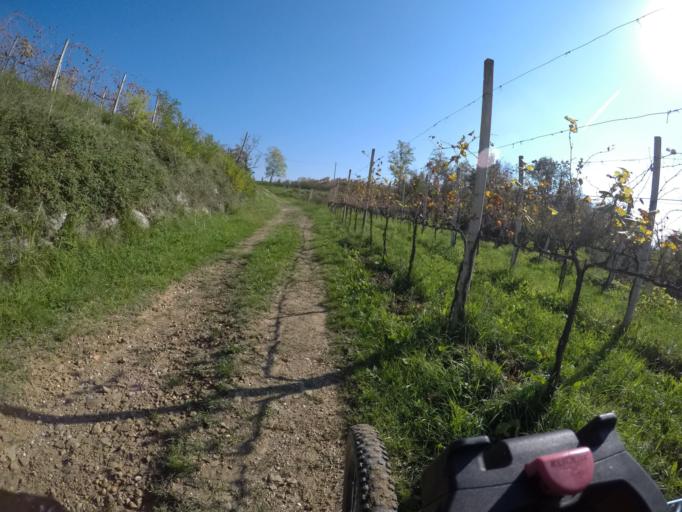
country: IT
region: Friuli Venezia Giulia
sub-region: Provincia di Udine
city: Manzano
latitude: 46.0067
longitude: 13.3768
